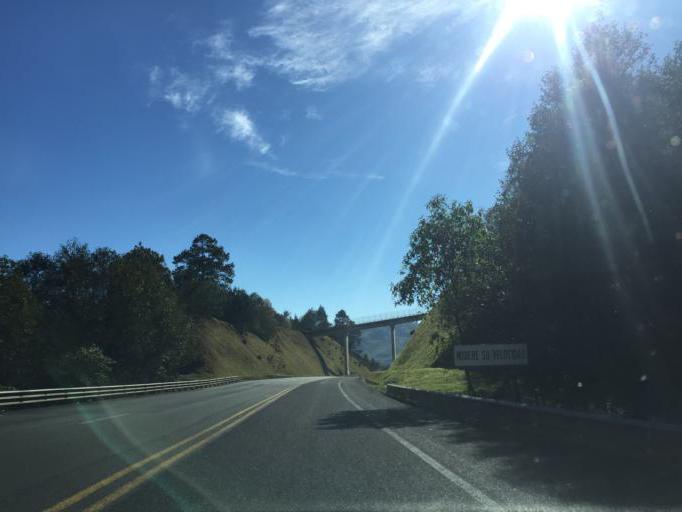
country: MX
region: Puebla
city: Huauchinango
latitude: 20.1402
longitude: -98.0441
